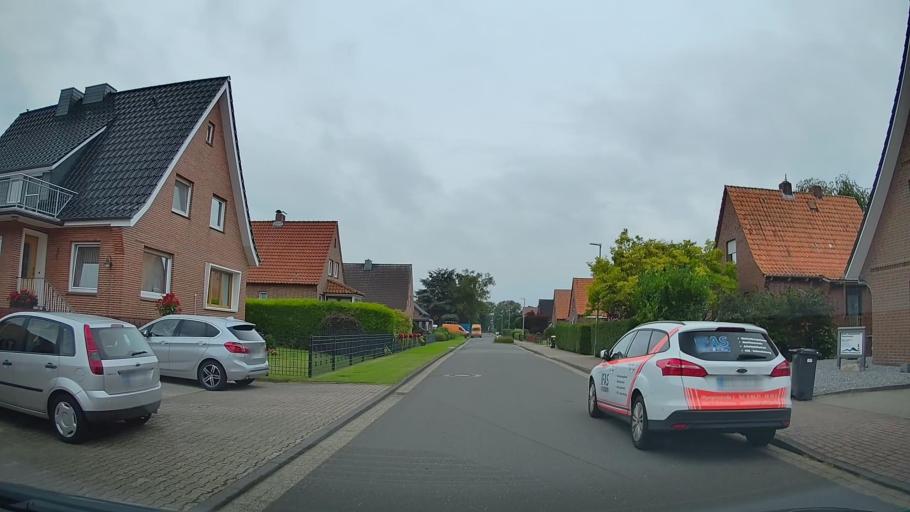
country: DE
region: Lower Saxony
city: Stade
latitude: 53.6703
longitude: 9.4827
